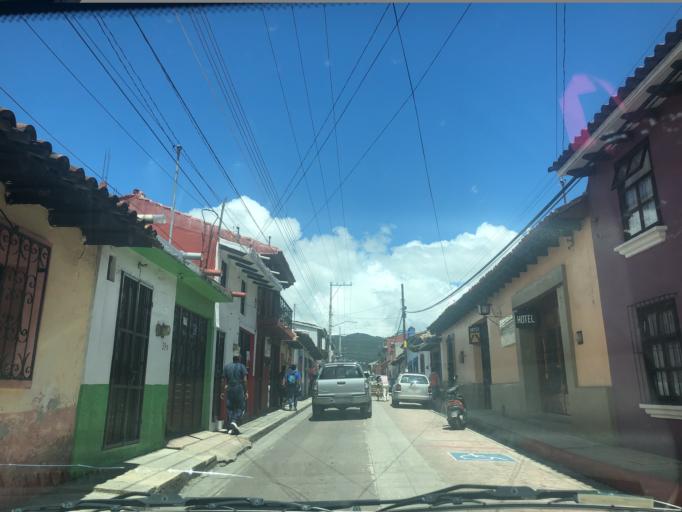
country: MX
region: Chiapas
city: San Cristobal de las Casas
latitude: 16.7312
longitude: -92.6391
